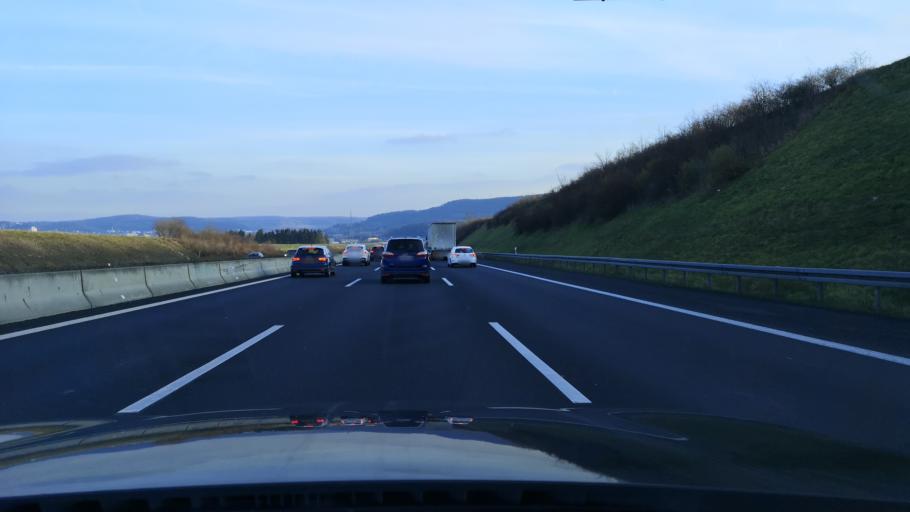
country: DE
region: Baden-Wuerttemberg
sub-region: Regierungsbezirk Stuttgart
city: Rutesheim
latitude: 48.7953
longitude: 8.9605
